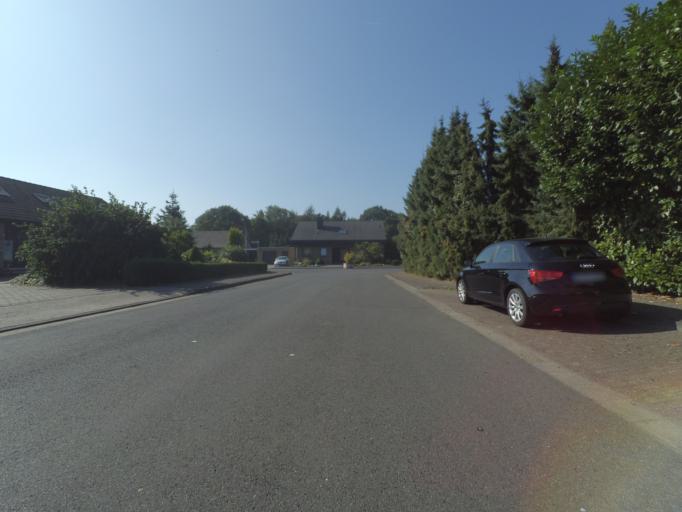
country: DE
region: North Rhine-Westphalia
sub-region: Regierungsbezirk Munster
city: Steinfurt
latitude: 52.1371
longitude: 7.3248
